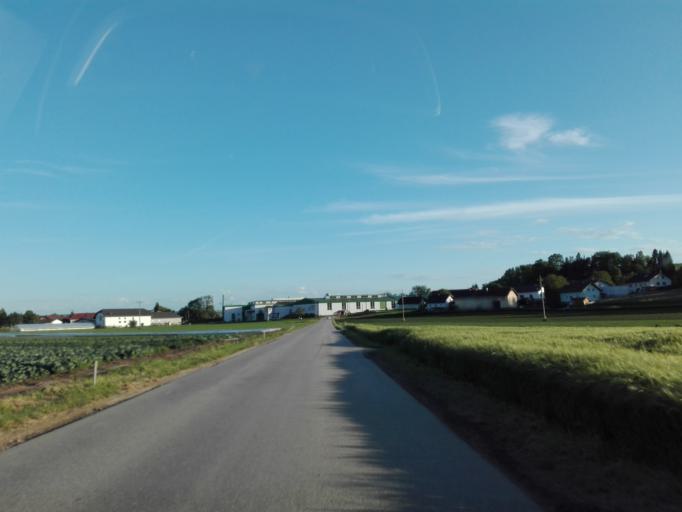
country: AT
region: Upper Austria
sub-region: Politischer Bezirk Urfahr-Umgebung
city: Feldkirchen an der Donau
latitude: 48.3148
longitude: 14.0041
